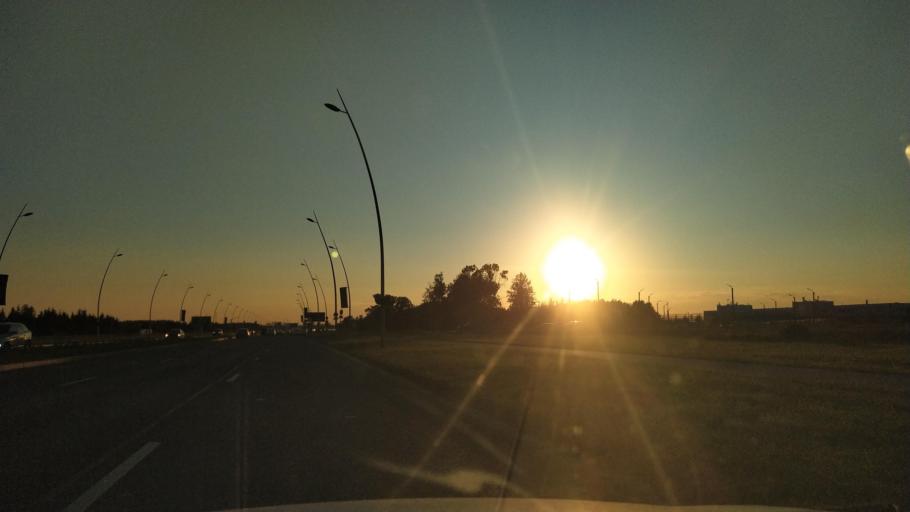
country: RU
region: St.-Petersburg
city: Aleksandrovskaya
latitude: 59.7934
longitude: 30.3050
